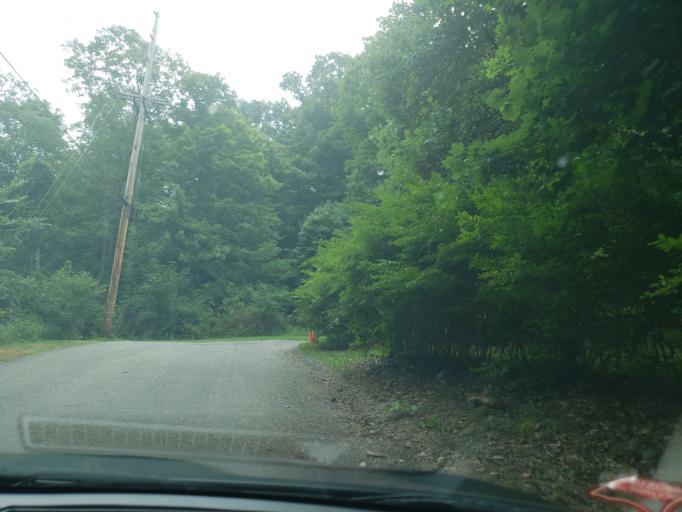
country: US
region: Pennsylvania
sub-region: Allegheny County
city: Ben Avon
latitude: 40.5184
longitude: -80.0857
